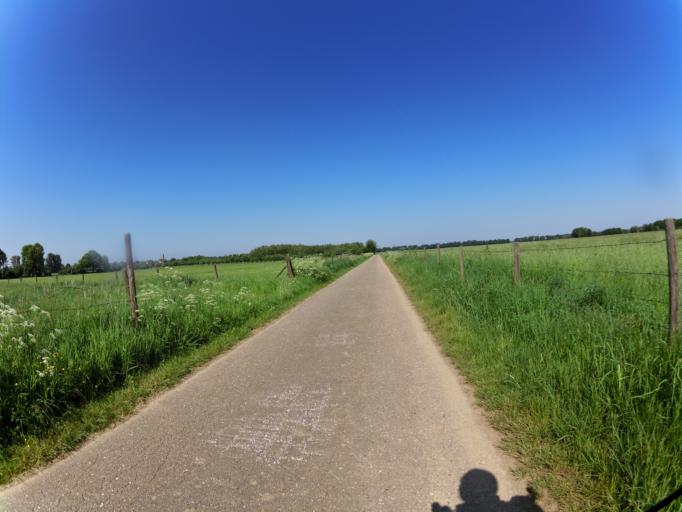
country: DE
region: North Rhine-Westphalia
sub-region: Regierungsbezirk Koln
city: Linnich
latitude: 51.0064
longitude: 6.2584
